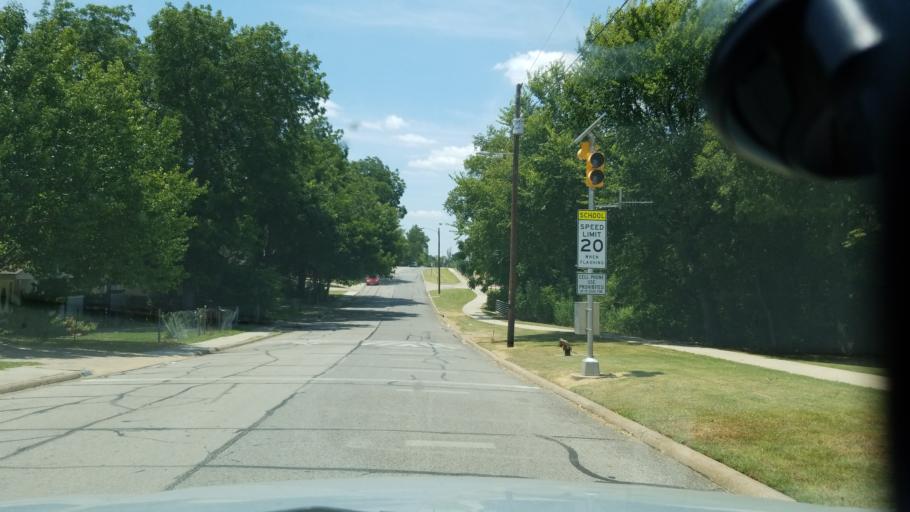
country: US
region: Texas
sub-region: Dallas County
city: Grand Prairie
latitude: 32.7558
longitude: -96.9667
